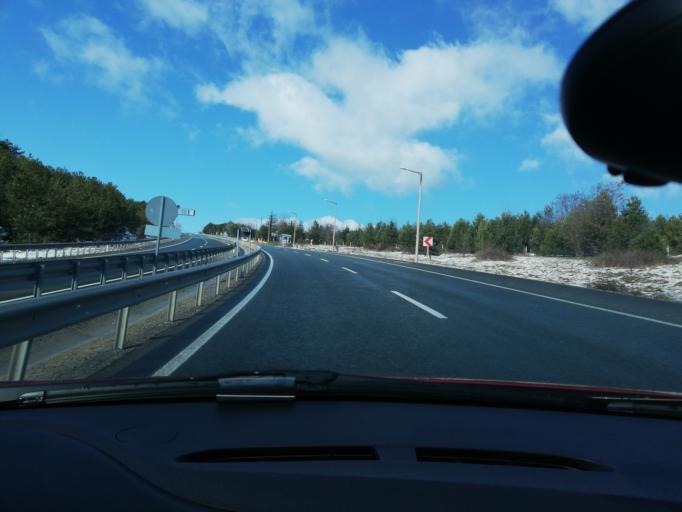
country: TR
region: Kastamonu
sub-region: Cide
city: Kastamonu
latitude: 41.3688
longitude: 33.7557
